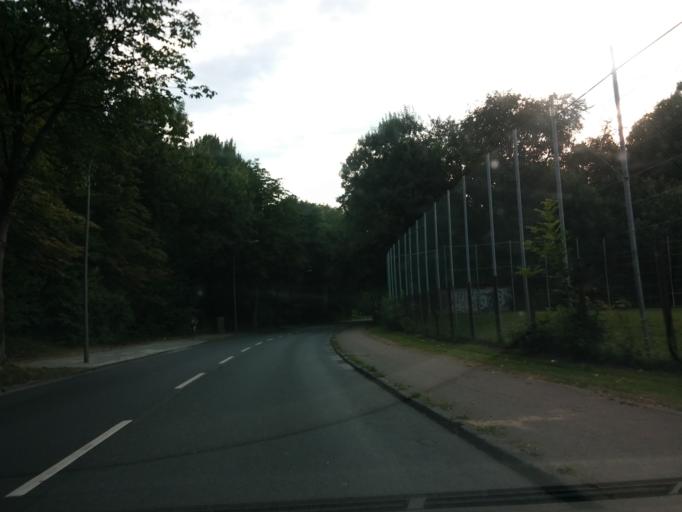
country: DE
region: North Rhine-Westphalia
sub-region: Regierungsbezirk Arnsberg
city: Bochum
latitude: 51.5055
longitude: 7.2385
